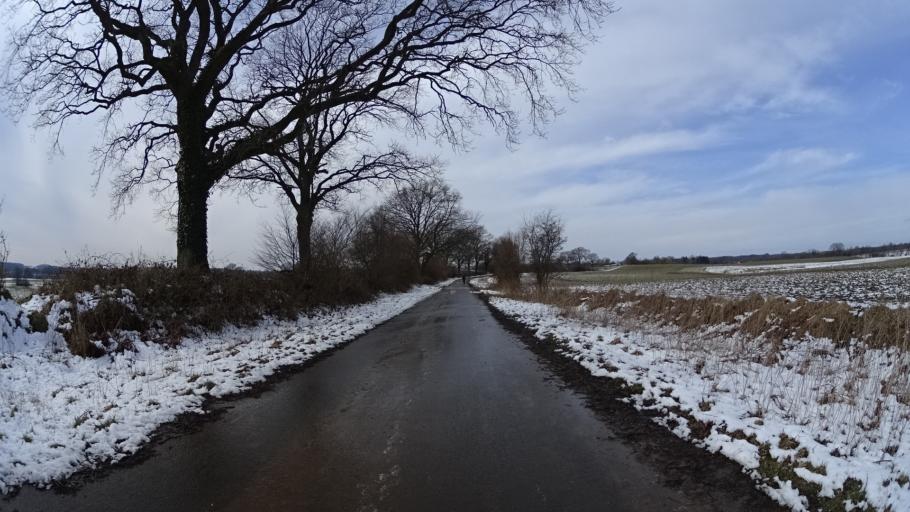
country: DE
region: Schleswig-Holstein
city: Loptin
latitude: 54.1678
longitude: 10.2260
